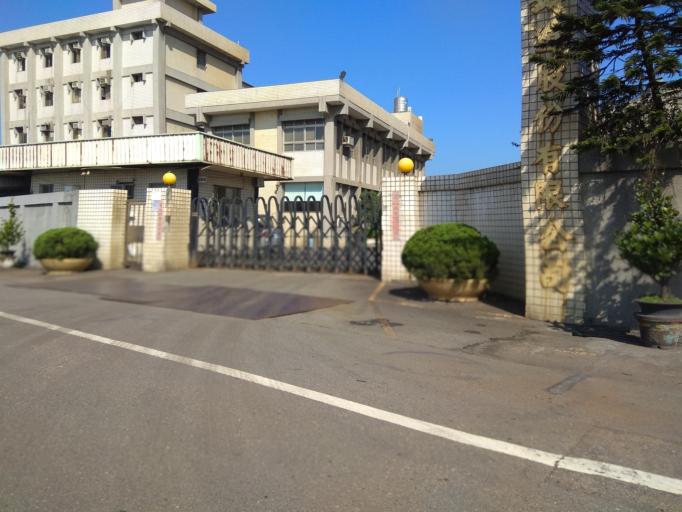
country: TW
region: Taiwan
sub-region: Hsinchu
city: Zhubei
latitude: 24.9805
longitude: 121.0382
